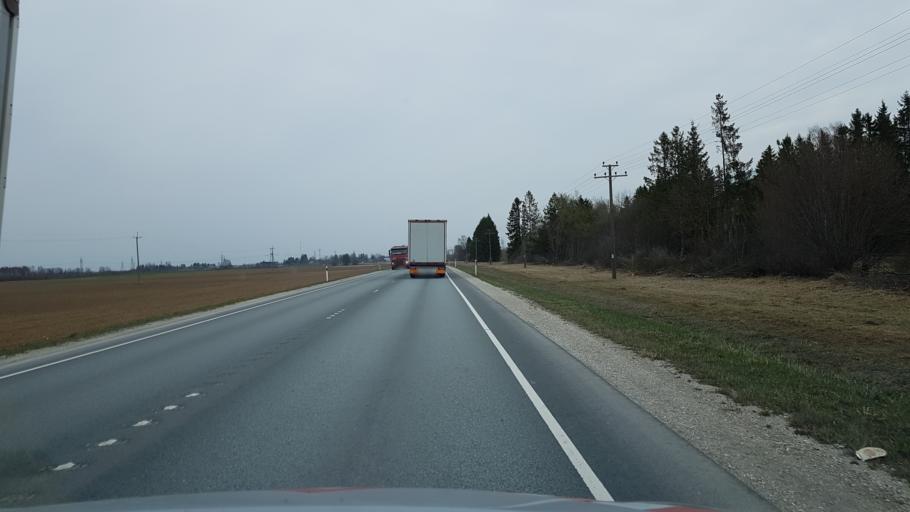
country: EE
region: Laeaene-Virumaa
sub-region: Rakvere linn
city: Rakvere
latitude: 59.3514
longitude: 26.3055
